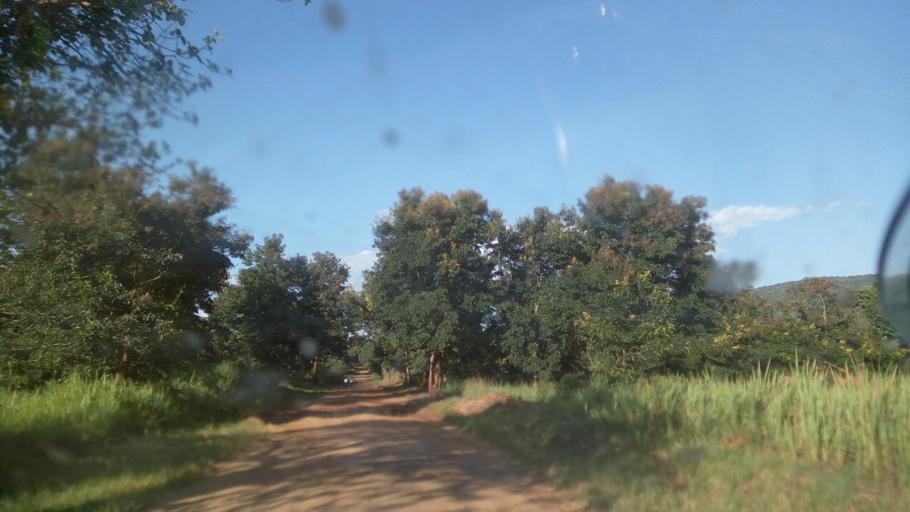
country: BI
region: Bururi
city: Rumonge
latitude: -4.2851
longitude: 28.9621
